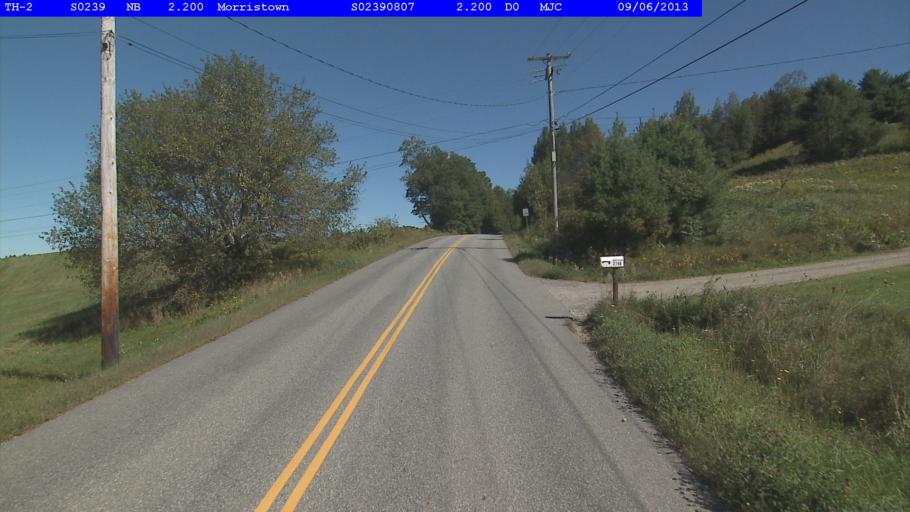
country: US
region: Vermont
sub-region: Lamoille County
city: Hyde Park
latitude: 44.5851
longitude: -72.6150
